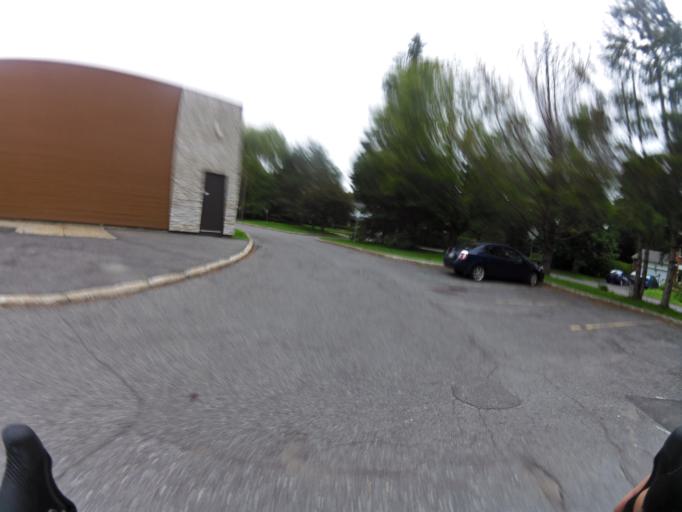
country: CA
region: Ontario
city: Ottawa
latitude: 45.3181
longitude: -75.7131
